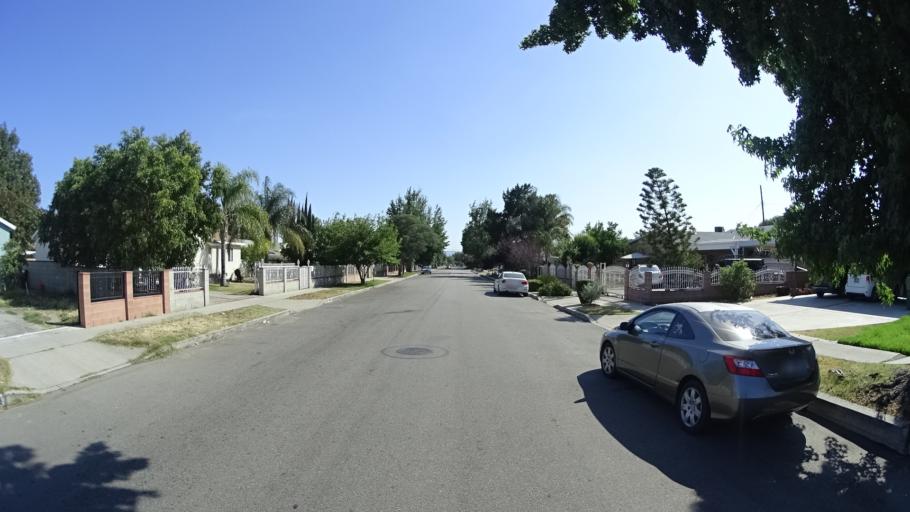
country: US
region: California
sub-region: Los Angeles County
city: Van Nuys
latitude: 34.2149
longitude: -118.4198
